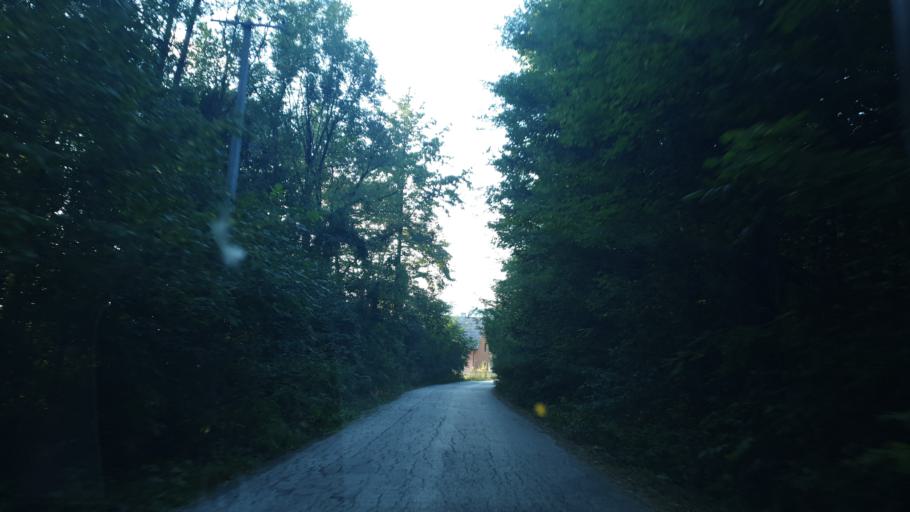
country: RS
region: Central Serbia
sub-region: Zlatiborski Okrug
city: Kosjeric
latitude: 43.9817
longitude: 20.0138
